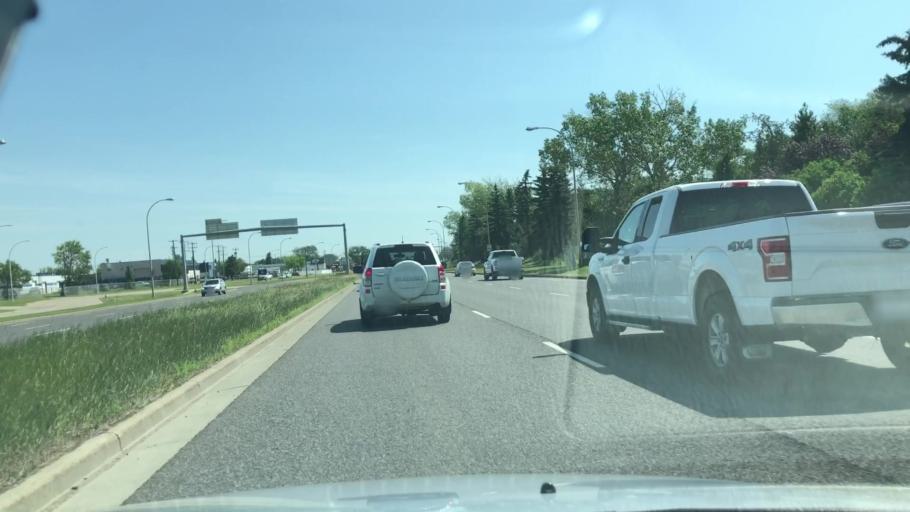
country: CA
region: Alberta
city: Edmonton
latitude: 53.5807
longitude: -113.5498
